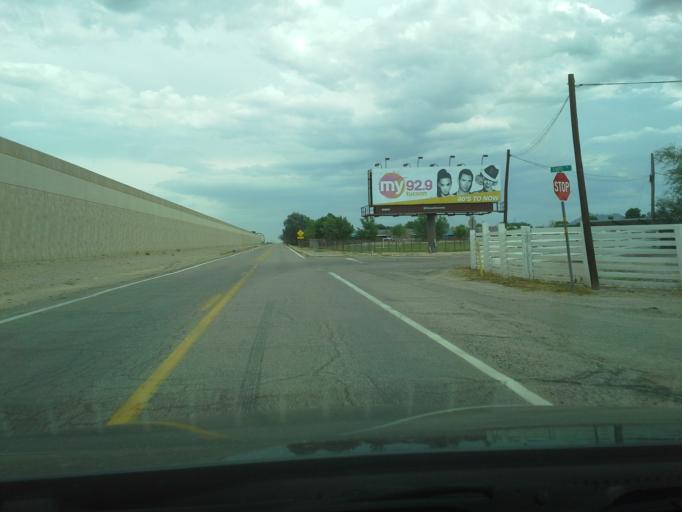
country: US
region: Arizona
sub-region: Pima County
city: Marana
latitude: 32.4571
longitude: -111.2098
